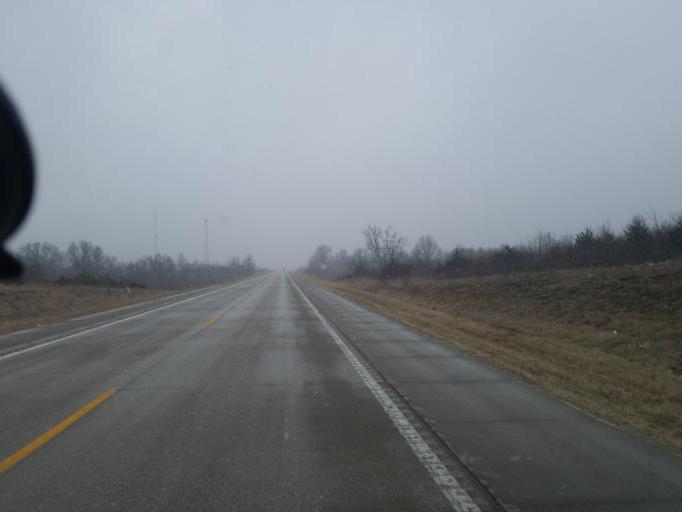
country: US
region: Missouri
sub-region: Adair County
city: Kirksville
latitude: 40.1821
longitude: -92.5522
